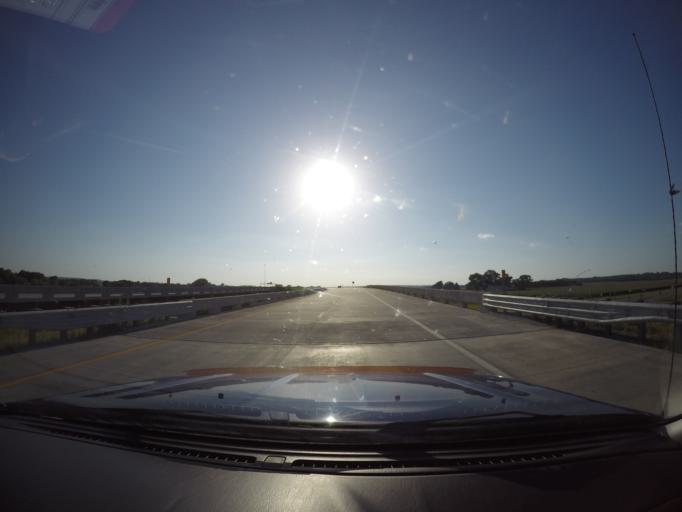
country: US
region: Kansas
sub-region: Shawnee County
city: Topeka
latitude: 39.0910
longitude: -95.7478
